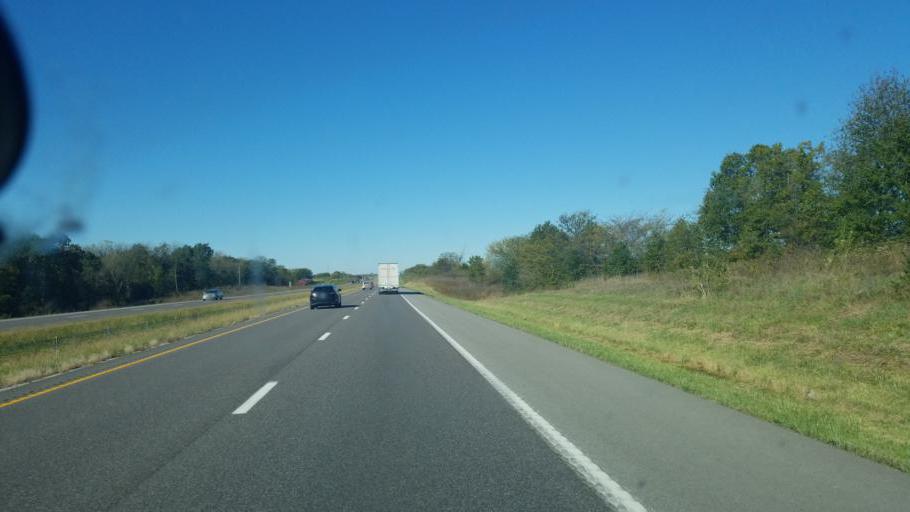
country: US
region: Missouri
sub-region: Saline County
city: Marshall
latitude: 38.9512
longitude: -93.0586
